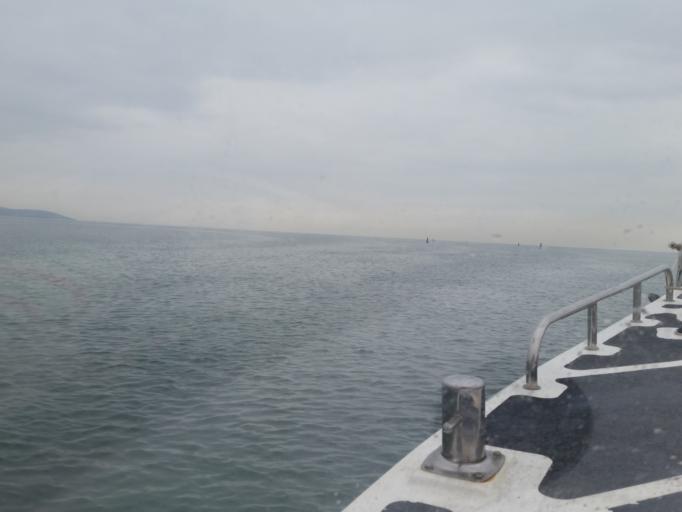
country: IE
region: Leinster
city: Malahide
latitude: 53.4518
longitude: -6.1361
